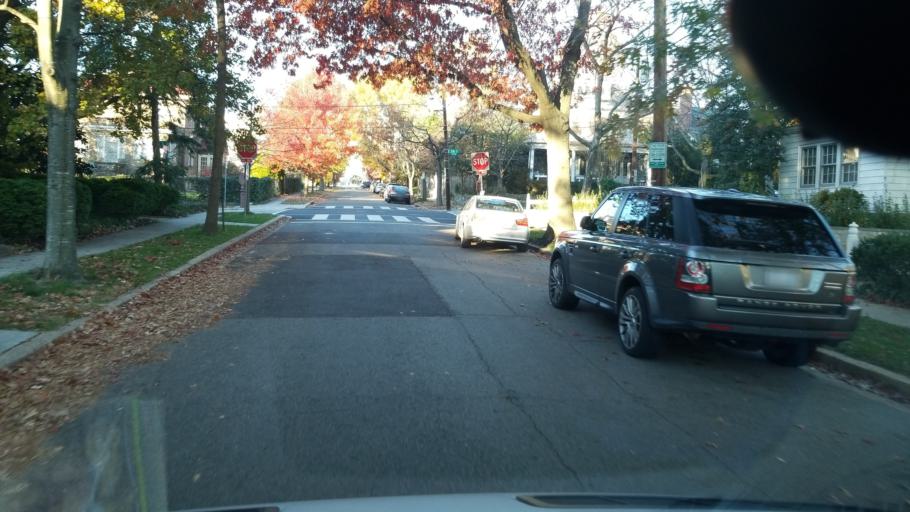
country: US
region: Maryland
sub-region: Montgomery County
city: Friendship Village
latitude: 38.9247
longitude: -77.0704
